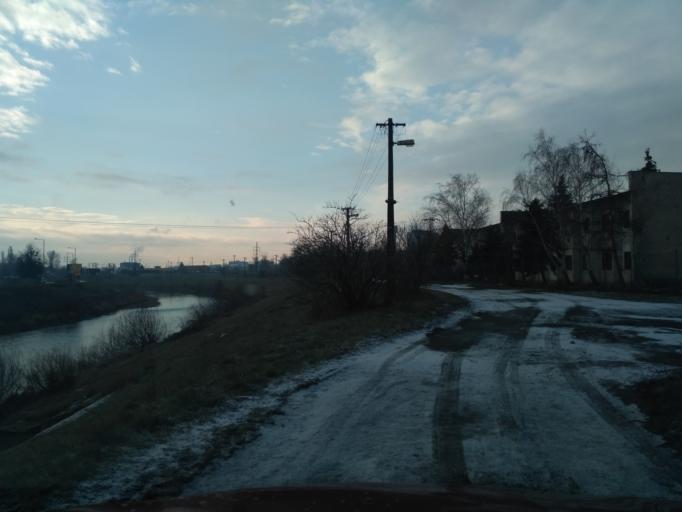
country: SK
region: Kosicky
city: Kosice
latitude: 48.7280
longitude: 21.2708
